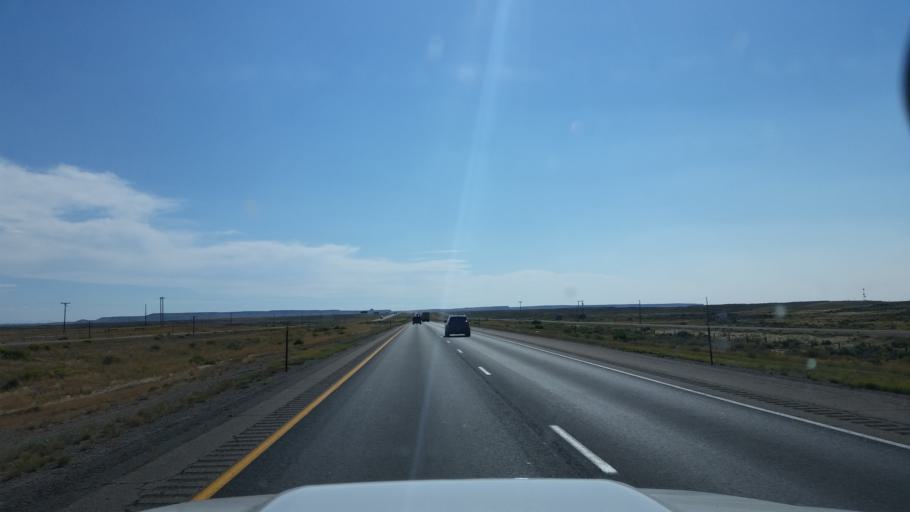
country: US
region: Wyoming
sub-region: Uinta County
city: Lyman
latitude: 41.5334
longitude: -109.9381
